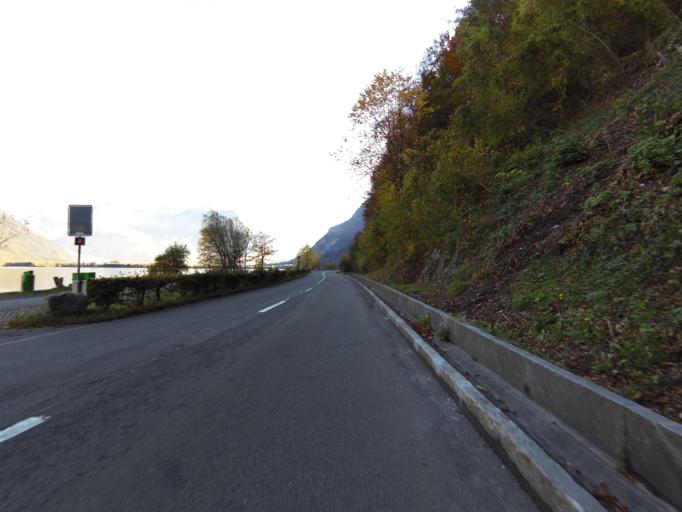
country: CH
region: Uri
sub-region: Uri
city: Flueelen
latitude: 46.9051
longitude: 8.5918
